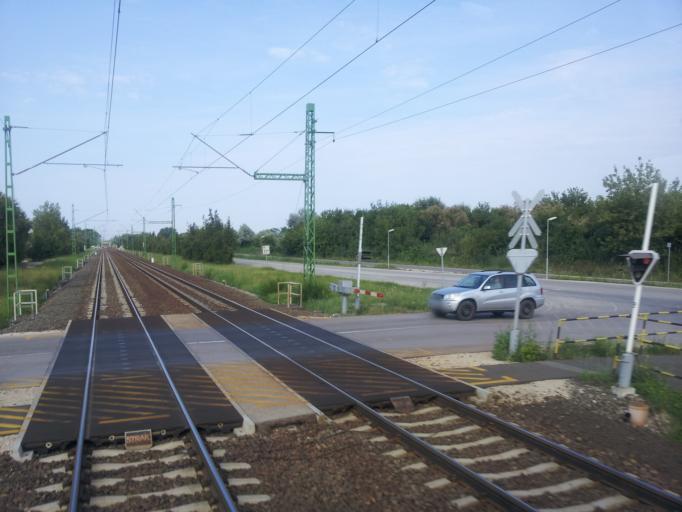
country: HU
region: Fejer
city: Gardony
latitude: 47.2121
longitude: 18.6359
